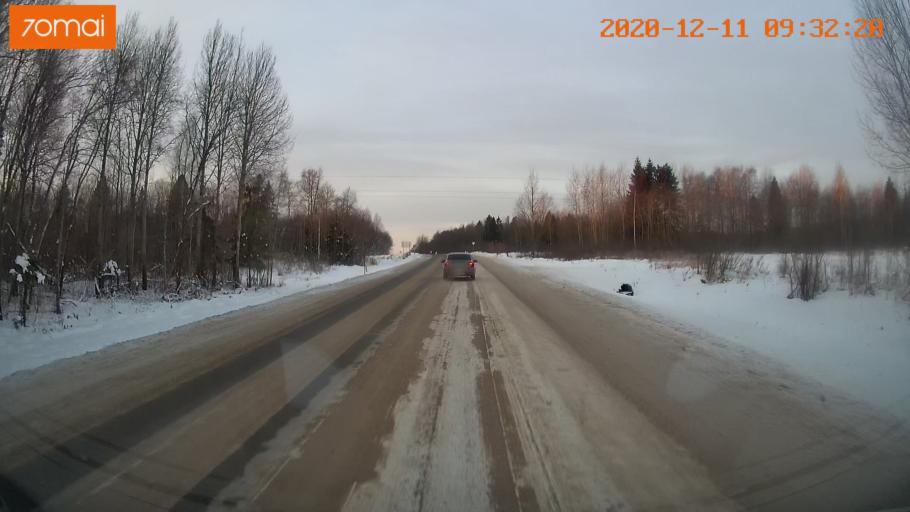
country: RU
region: Vologda
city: Vologda
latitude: 59.1238
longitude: 39.9698
